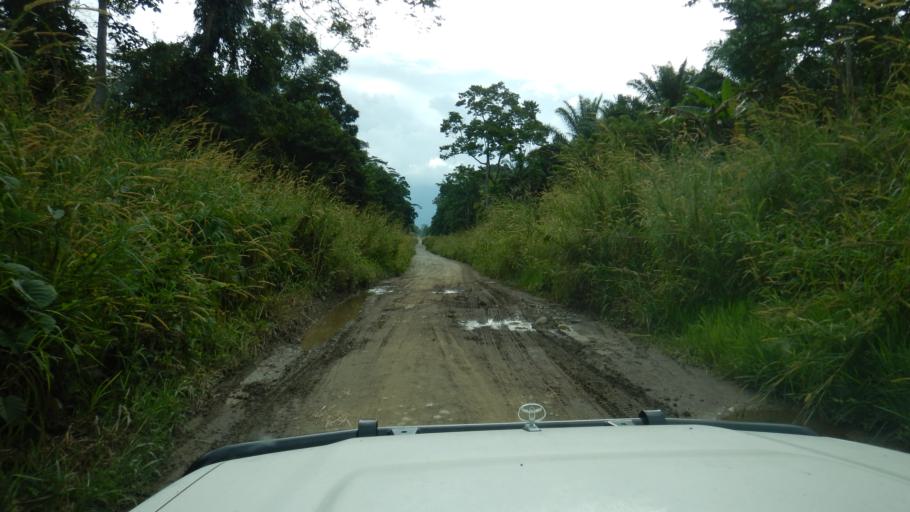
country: PG
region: Northern Province
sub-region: Sohe
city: Kokoda
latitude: -8.9184
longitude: 147.7837
